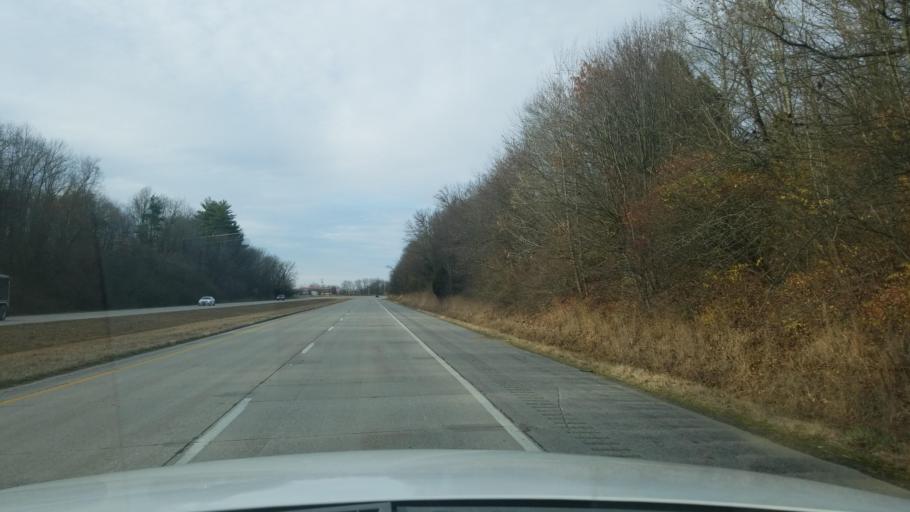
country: US
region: Indiana
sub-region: Vanderburgh County
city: Evansville
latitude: 37.9450
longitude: -87.7117
